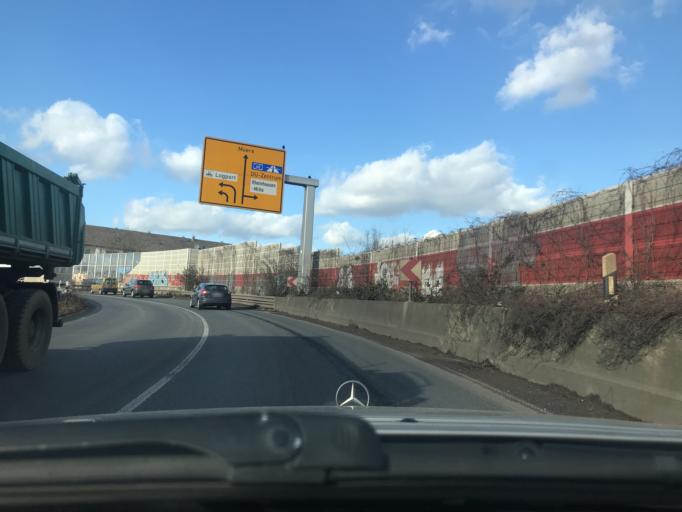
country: DE
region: North Rhine-Westphalia
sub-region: Regierungsbezirk Dusseldorf
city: Hochfeld
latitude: 51.3973
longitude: 6.7129
